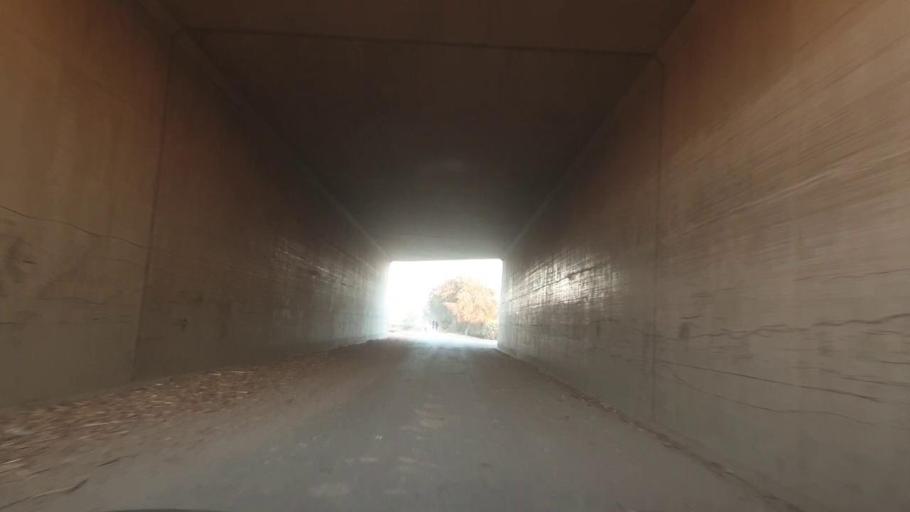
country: PK
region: Sindh
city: Ghotki
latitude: 28.0387
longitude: 69.3174
